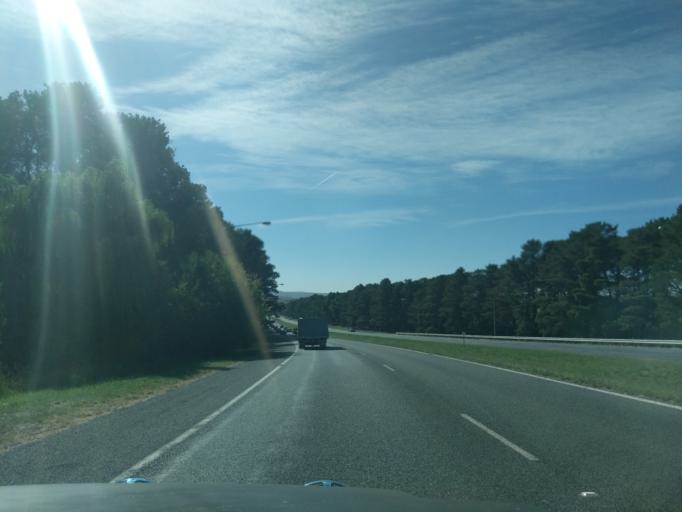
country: AU
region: Australian Capital Territory
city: Forrest
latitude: -35.3455
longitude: 149.1460
